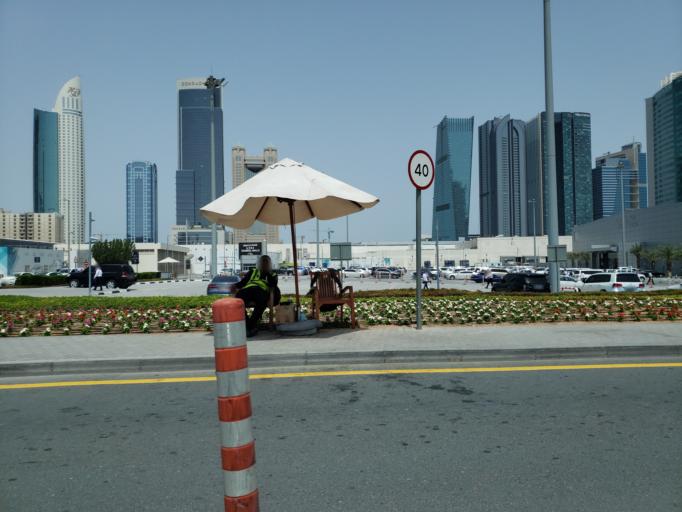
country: AE
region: Ash Shariqah
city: Sharjah
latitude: 25.2233
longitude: 55.2902
